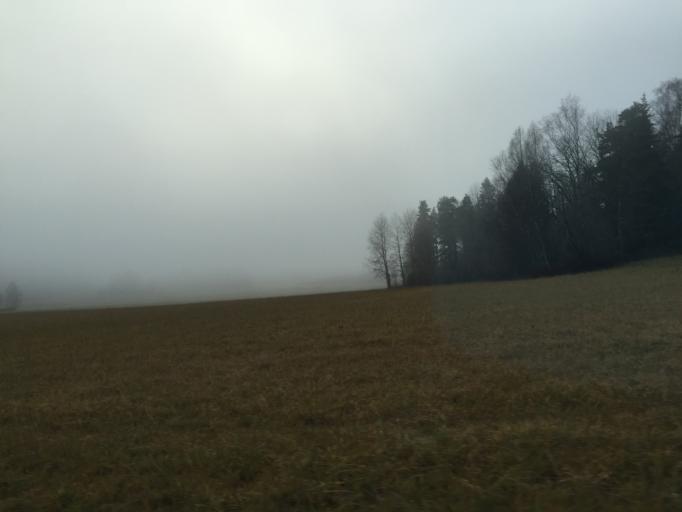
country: SE
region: Stockholm
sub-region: Botkyrka Kommun
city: Varsta
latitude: 59.1117
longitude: 17.8637
